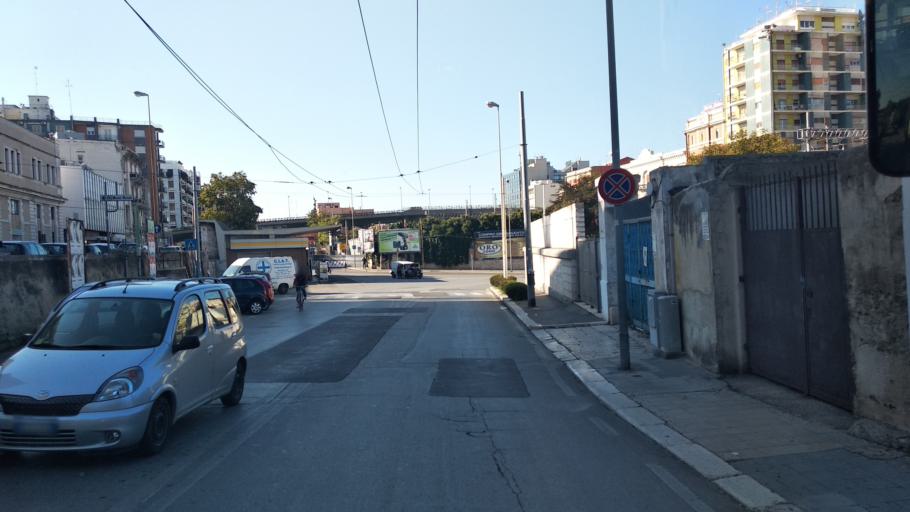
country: IT
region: Apulia
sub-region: Provincia di Bari
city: Bari
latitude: 41.1175
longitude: 16.8753
